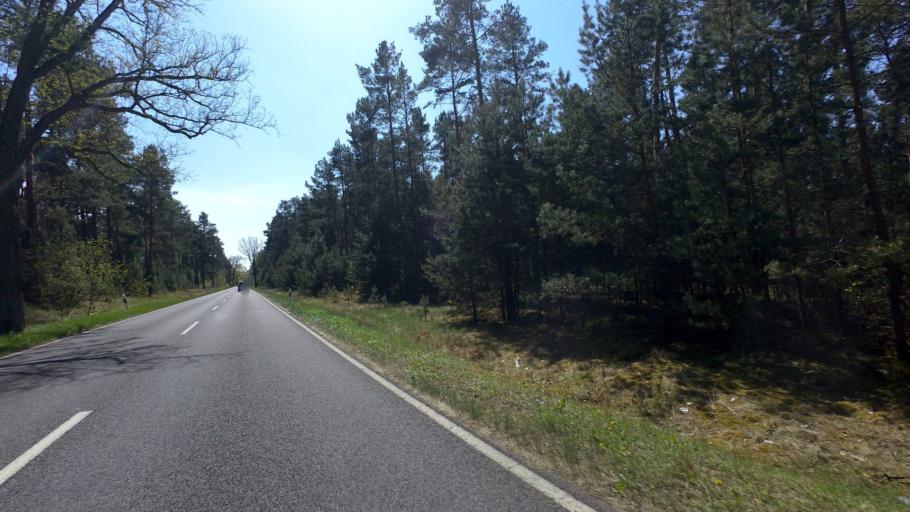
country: DE
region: Brandenburg
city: Halbe
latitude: 52.1239
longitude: 13.7560
